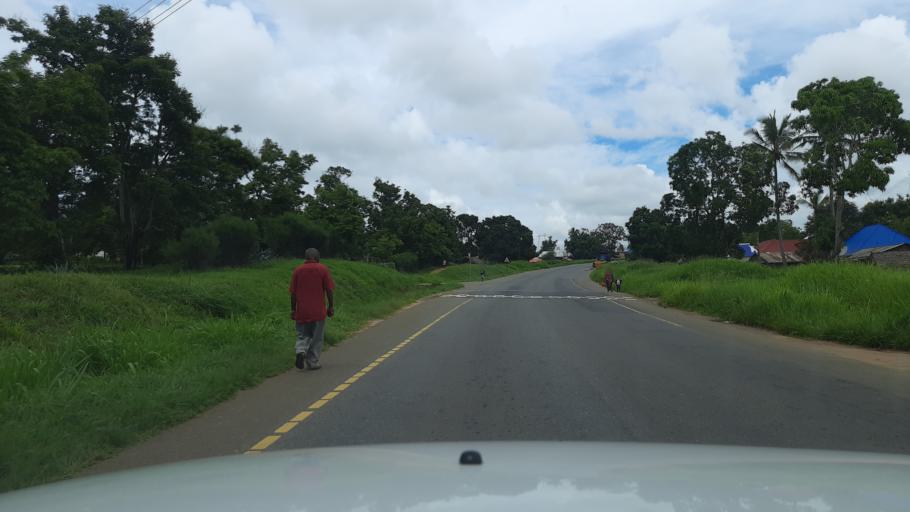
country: TZ
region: Tanga
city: Chanika
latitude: -5.9125
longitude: 38.2341
